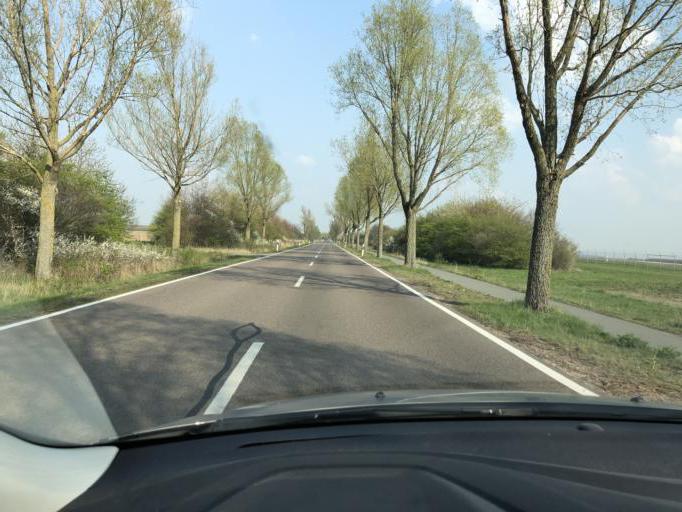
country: DE
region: Saxony
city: Zwochau
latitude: 51.4363
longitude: 12.2584
